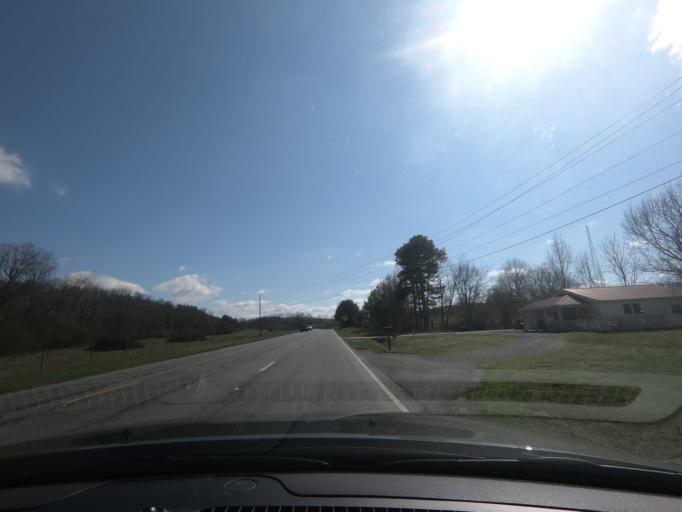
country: US
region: Georgia
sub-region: Bartow County
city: Rydal
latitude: 34.3917
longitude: -84.7066
